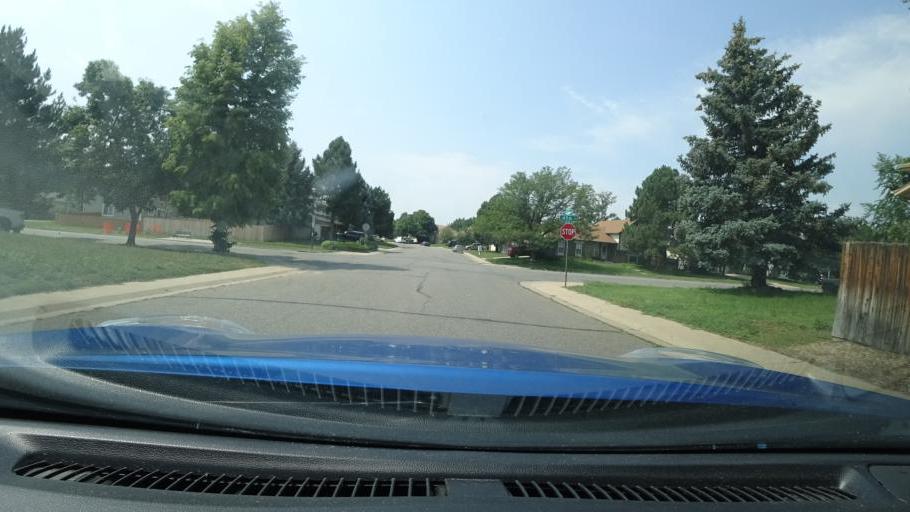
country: US
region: Colorado
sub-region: Adams County
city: Aurora
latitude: 39.7777
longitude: -104.7638
